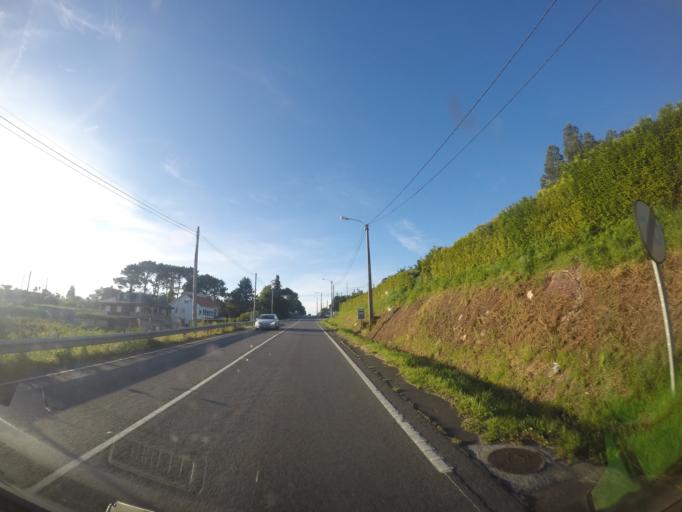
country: ES
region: Galicia
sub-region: Provincia da Coruna
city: Noia
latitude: 42.7698
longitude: -8.9366
